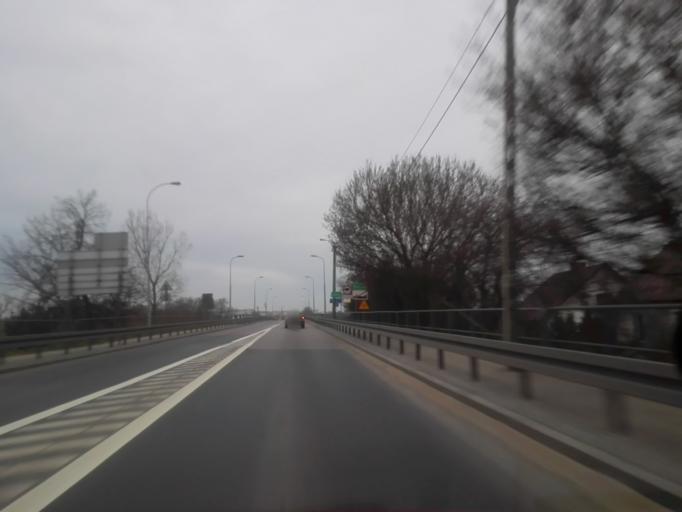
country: PL
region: Podlasie
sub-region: Powiat lomzynski
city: Piatnica
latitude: 53.1943
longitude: 22.0944
